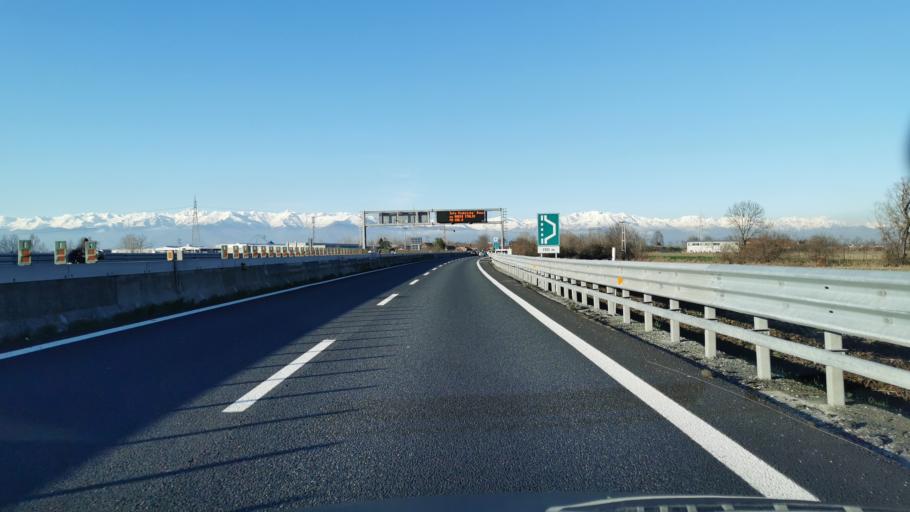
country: IT
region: Piedmont
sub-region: Provincia di Torino
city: Borgaro Torinese
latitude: 45.1449
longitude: 7.6891
